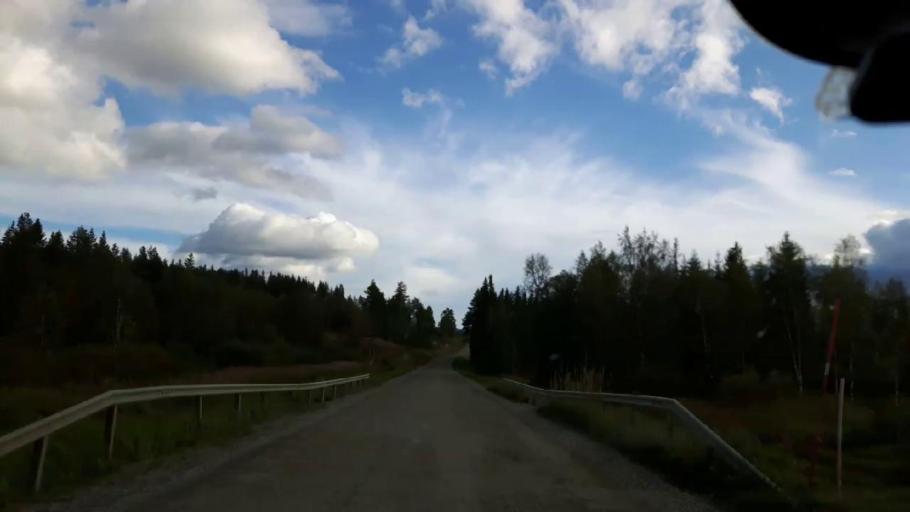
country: SE
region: Jaemtland
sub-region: Stroemsunds Kommun
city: Stroemsund
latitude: 63.3026
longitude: 15.6028
